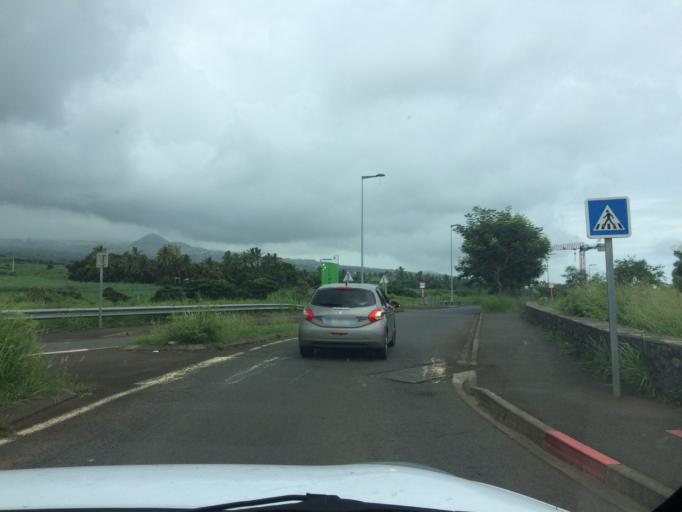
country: RE
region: Reunion
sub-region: Reunion
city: Saint-Pierre
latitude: -21.3367
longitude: 55.4876
